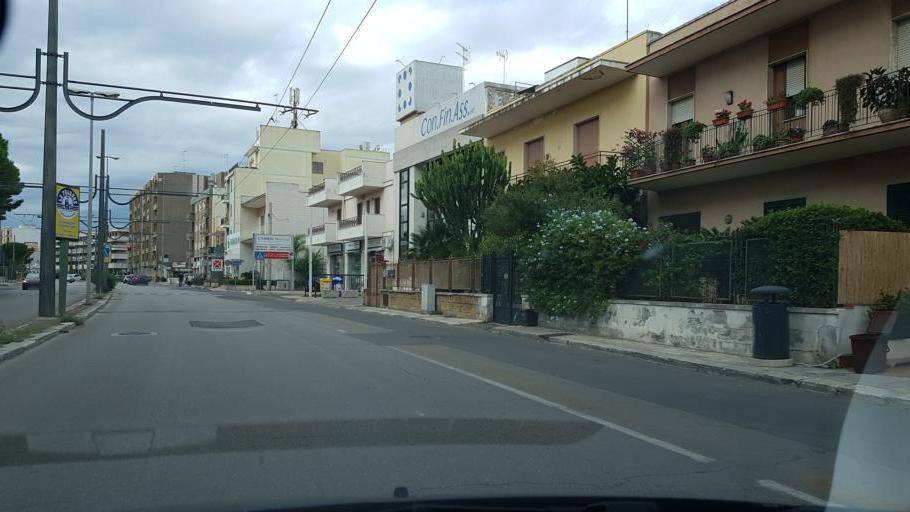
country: IT
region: Apulia
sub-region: Provincia di Lecce
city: Lecce
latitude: 40.3601
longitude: 18.1815
